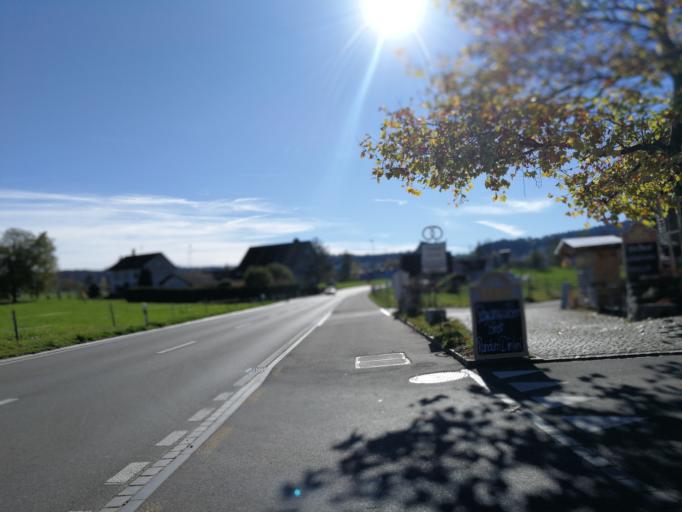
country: CH
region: Zurich
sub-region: Bezirk Meilen
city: Oetwil am See
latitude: 47.2790
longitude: 8.7267
